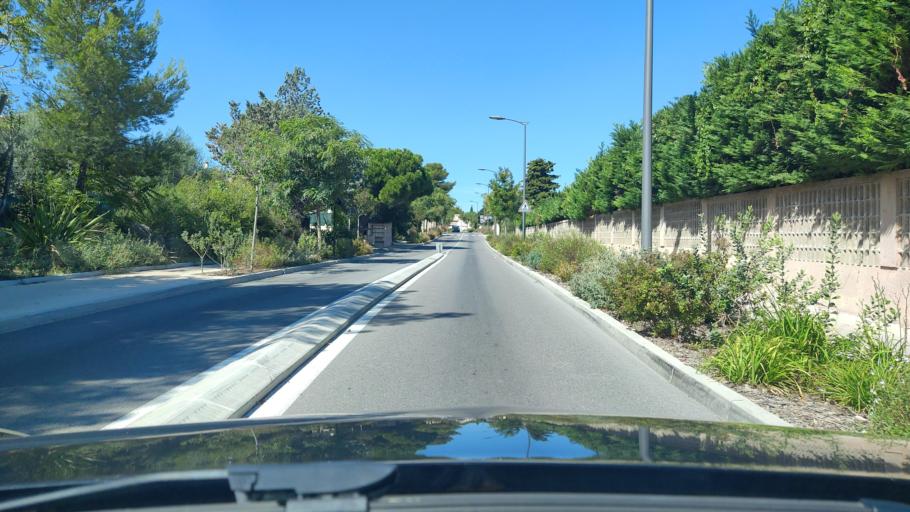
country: FR
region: Provence-Alpes-Cote d'Azur
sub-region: Departement du Var
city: Sanary-sur-Mer
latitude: 43.1299
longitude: 5.7942
